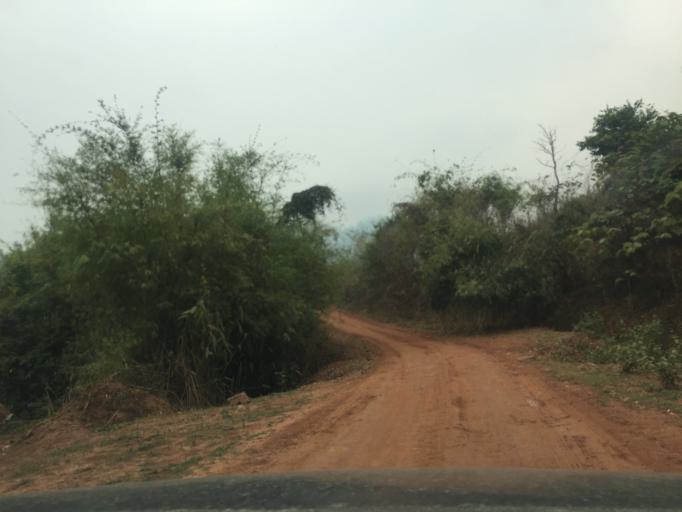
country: TH
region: Nan
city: Bo Kluea
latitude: 18.8506
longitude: 101.4171
